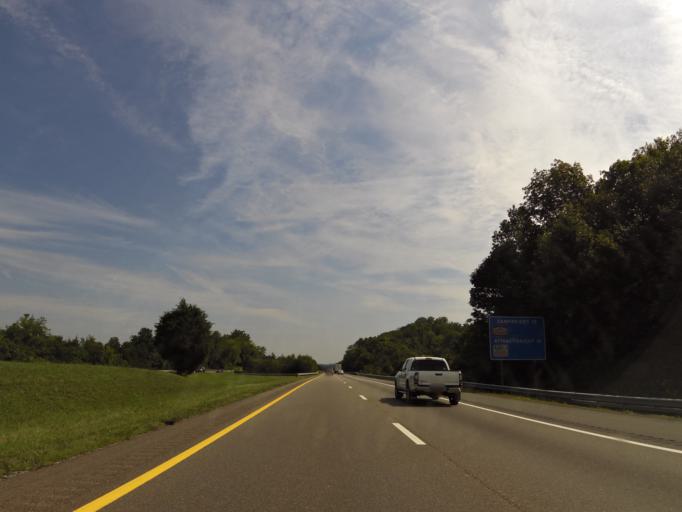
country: US
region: Tennessee
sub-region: Hamblen County
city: Morristown
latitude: 36.1827
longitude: -83.1947
